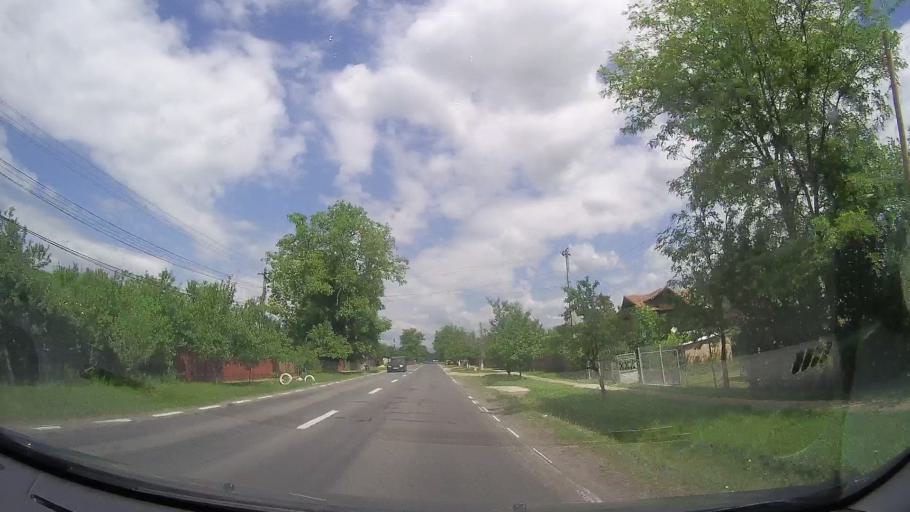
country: RO
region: Prahova
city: Drajna de Jos
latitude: 45.2152
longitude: 26.0372
